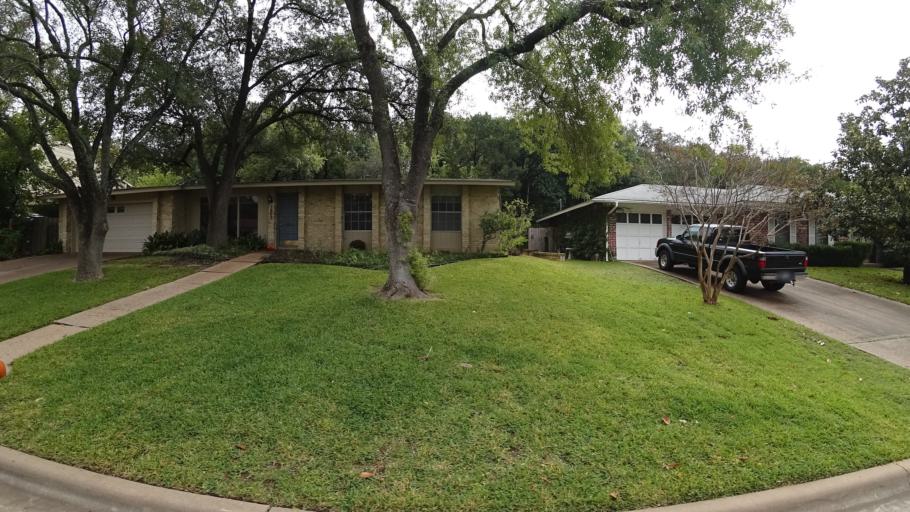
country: US
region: Texas
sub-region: Travis County
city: Rollingwood
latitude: 30.2572
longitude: -97.7800
